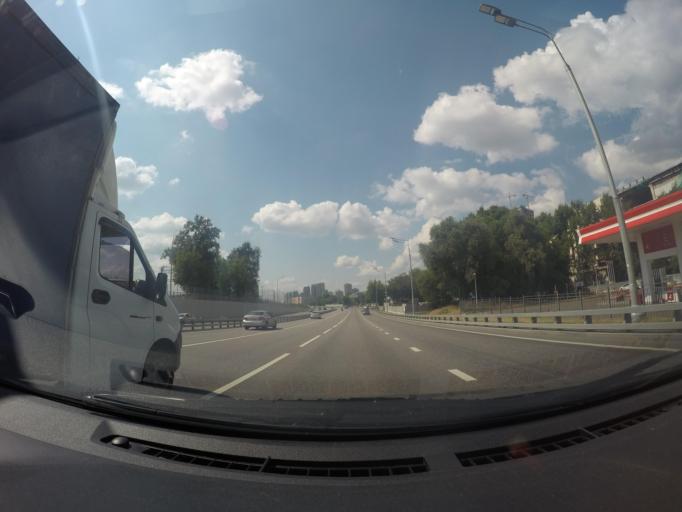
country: RU
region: Moscow
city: Leonovo
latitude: 55.8444
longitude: 37.6550
